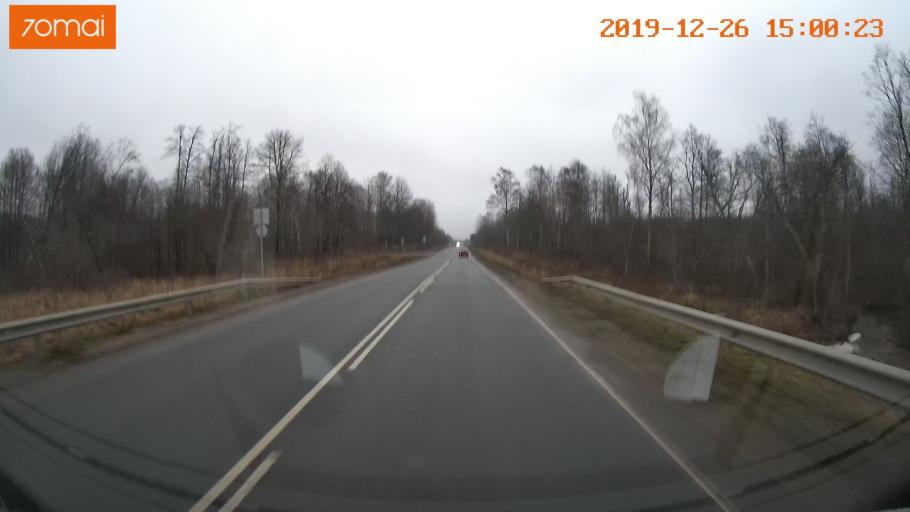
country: RU
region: Jaroslavl
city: Rybinsk
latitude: 58.2469
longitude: 38.8509
